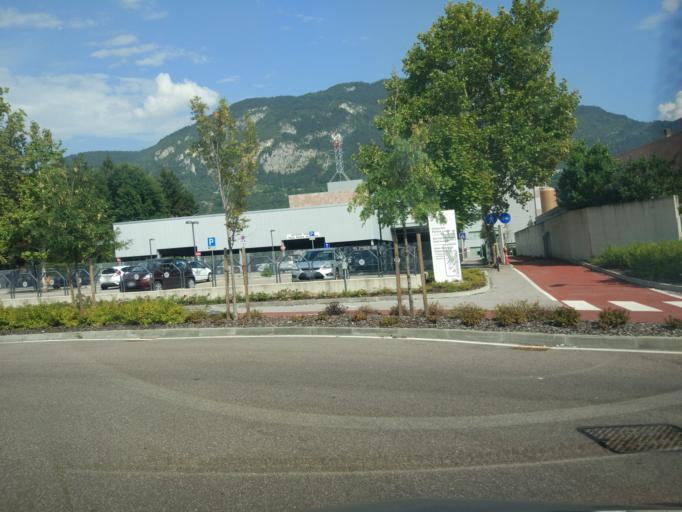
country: IT
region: Trentino-Alto Adige
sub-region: Provincia di Trento
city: Trento
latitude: 46.0904
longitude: 11.1086
